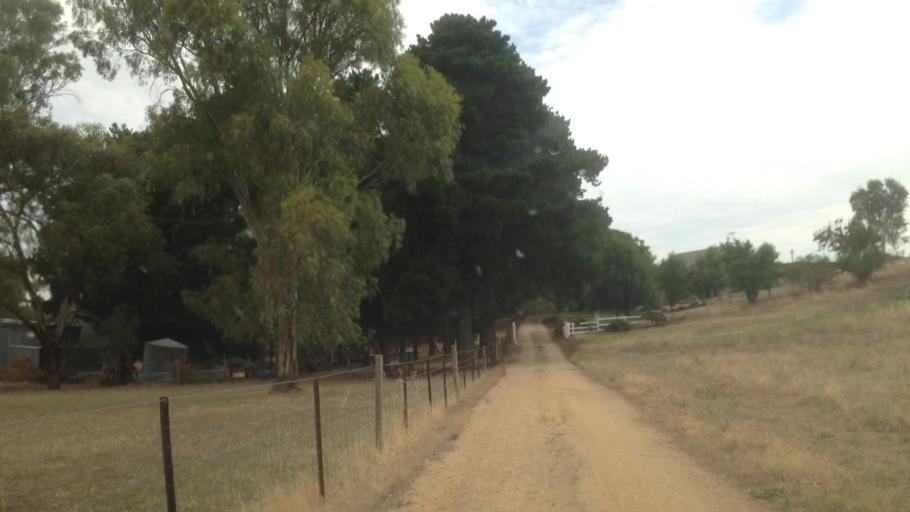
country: AU
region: South Australia
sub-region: Barossa
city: Williamstown
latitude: -34.6769
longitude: 138.8827
